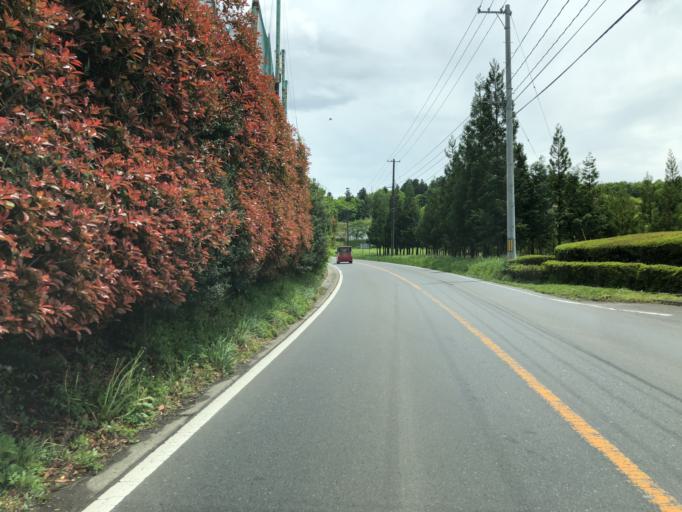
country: JP
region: Fukushima
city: Ishikawa
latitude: 37.0790
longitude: 140.3578
